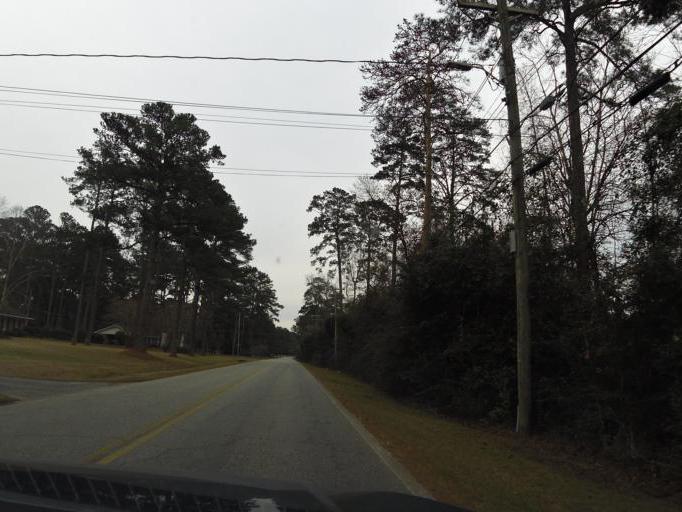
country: US
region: Georgia
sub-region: Thomas County
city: Thomasville
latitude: 30.8178
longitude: -83.9527
